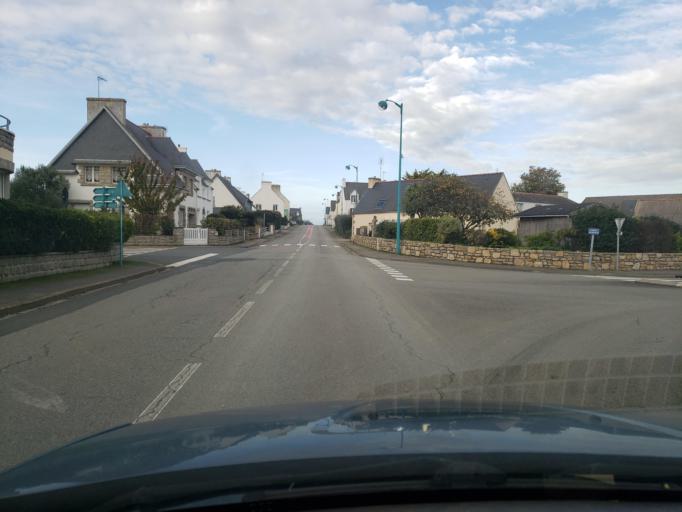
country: FR
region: Brittany
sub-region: Departement du Finistere
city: Guilvinec
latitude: 47.7989
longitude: -4.2652
